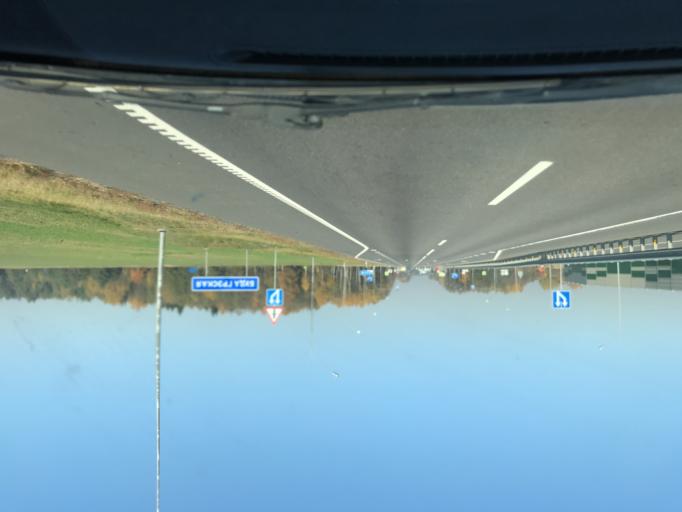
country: BY
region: Minsk
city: Slutsk
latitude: 53.2700
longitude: 27.5502
